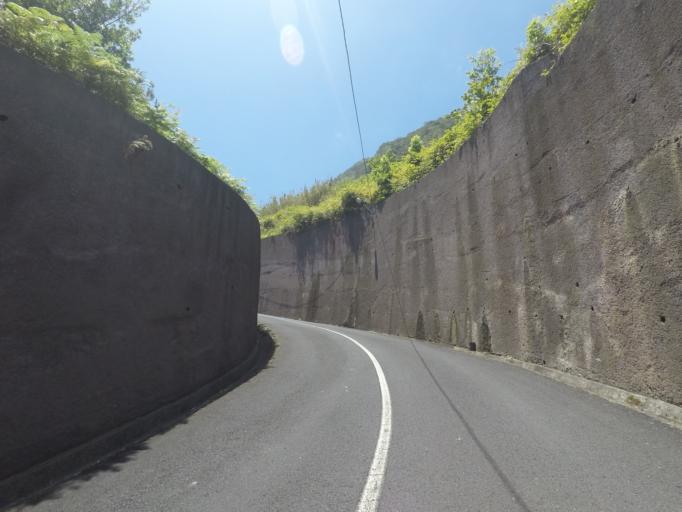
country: PT
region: Madeira
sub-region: Porto Moniz
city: Porto Moniz
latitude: 32.8312
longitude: -17.1325
